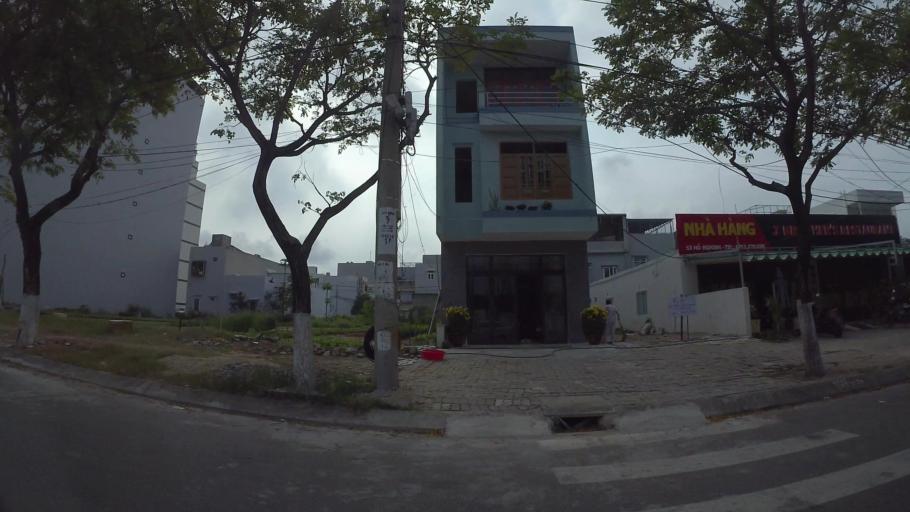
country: VN
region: Da Nang
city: Son Tra
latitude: 16.0775
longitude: 108.2428
